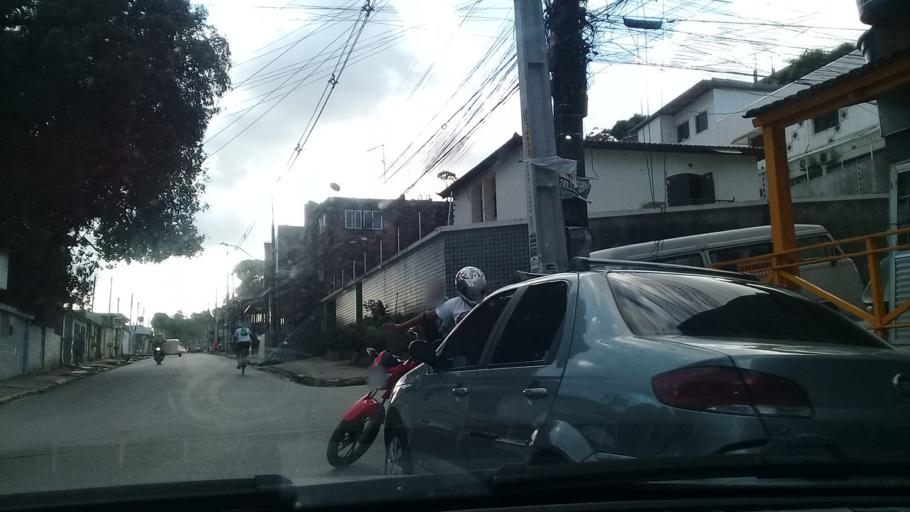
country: BR
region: Pernambuco
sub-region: Jaboatao Dos Guararapes
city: Jaboatao
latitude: -8.1369
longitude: -34.9382
